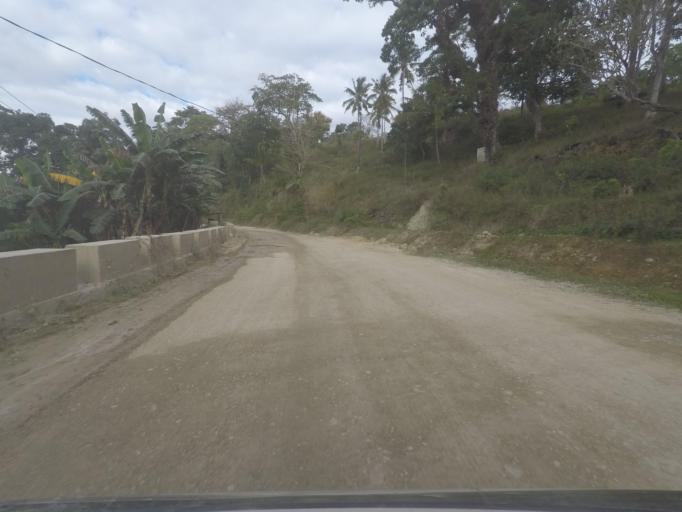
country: TL
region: Baucau
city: Venilale
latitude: -8.6013
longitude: 126.3847
